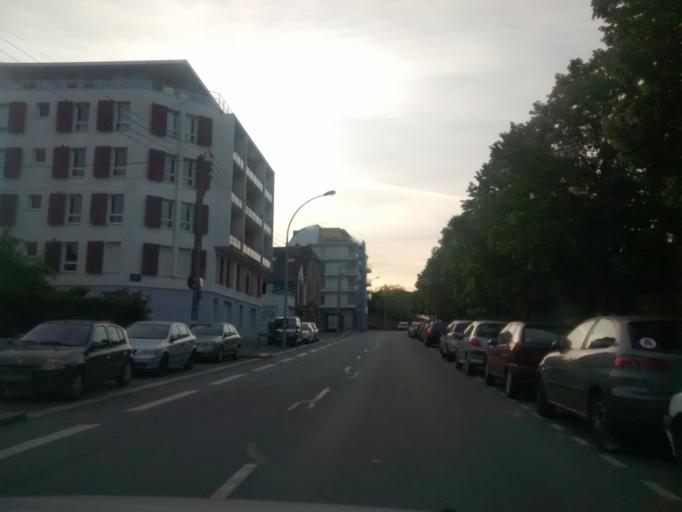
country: FR
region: Brittany
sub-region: Departement d'Ille-et-Vilaine
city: Rennes
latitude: 48.1147
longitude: -1.6544
